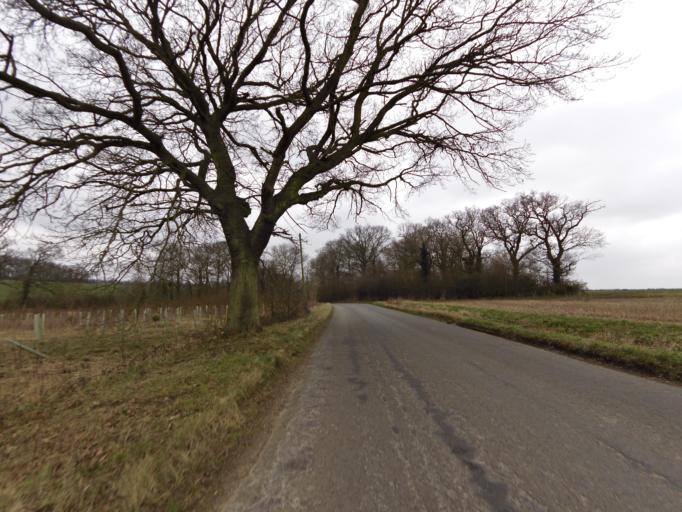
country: GB
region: England
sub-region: Suffolk
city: Cookley
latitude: 52.2870
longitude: 1.4626
